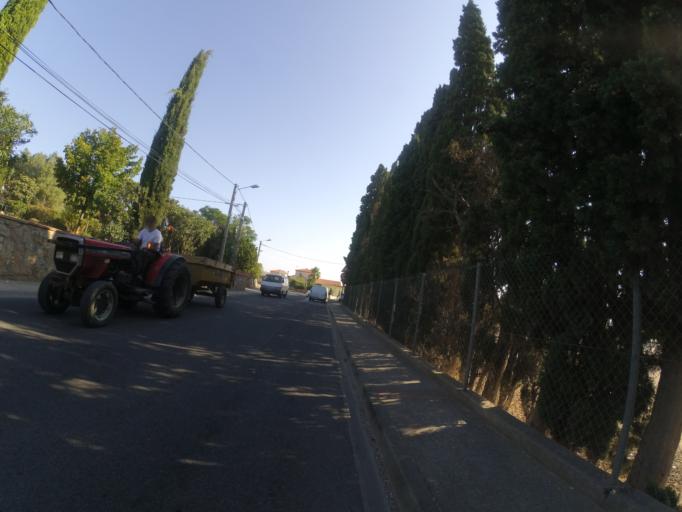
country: FR
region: Languedoc-Roussillon
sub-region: Departement des Pyrenees-Orientales
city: Baixas
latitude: 42.7535
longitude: 2.8131
